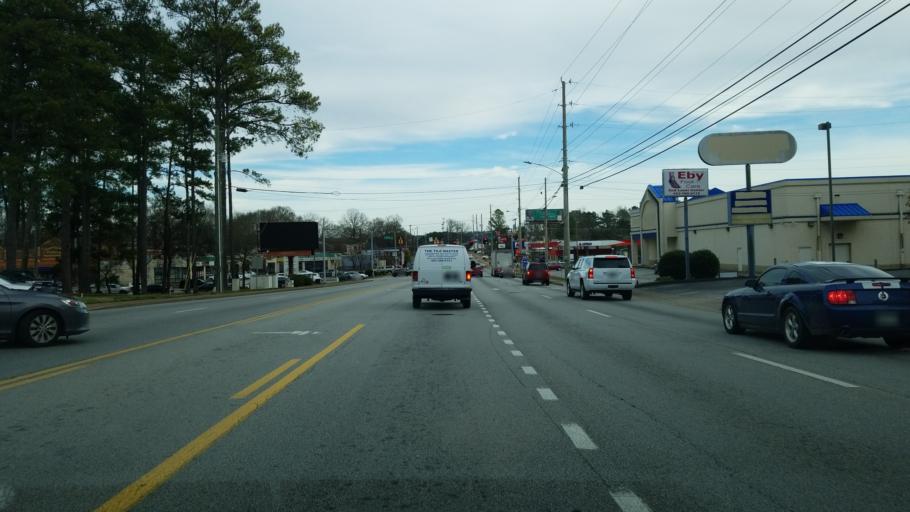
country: US
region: Tennessee
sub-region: Hamilton County
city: East Brainerd
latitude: 35.0160
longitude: -85.1649
